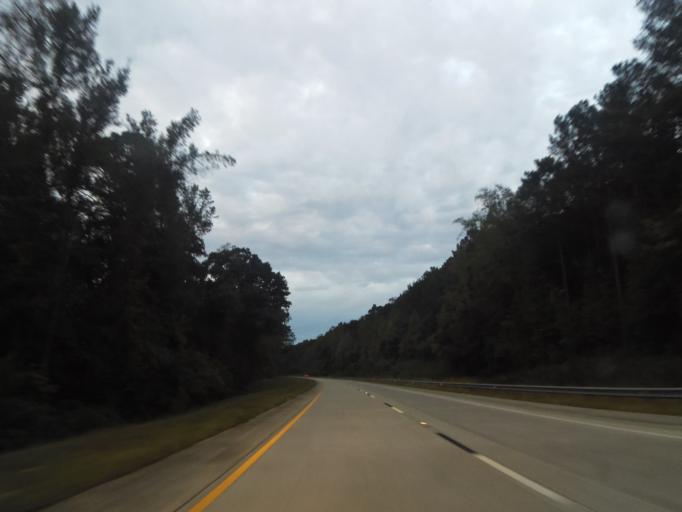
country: US
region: Alabama
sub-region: Etowah County
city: Gadsden
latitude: 34.0525
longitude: -86.0433
